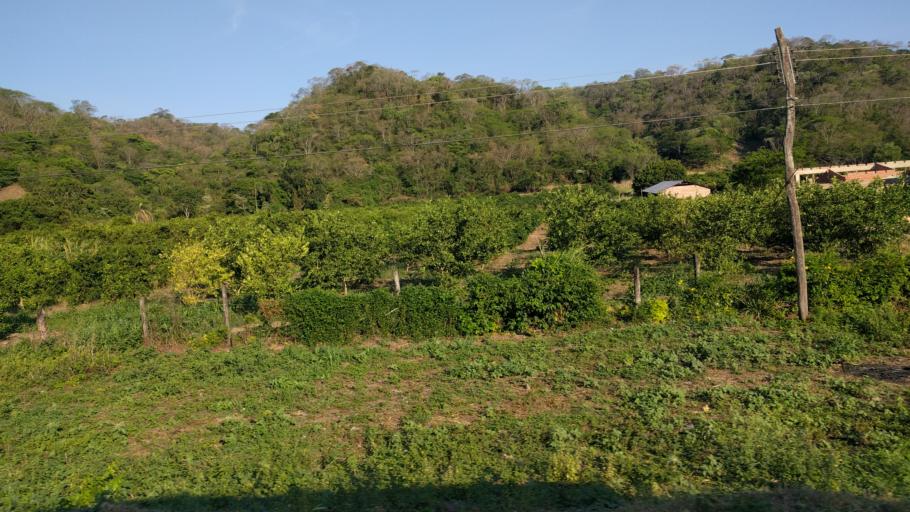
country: BO
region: Santa Cruz
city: Jorochito
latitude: -18.0750
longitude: -63.4442
